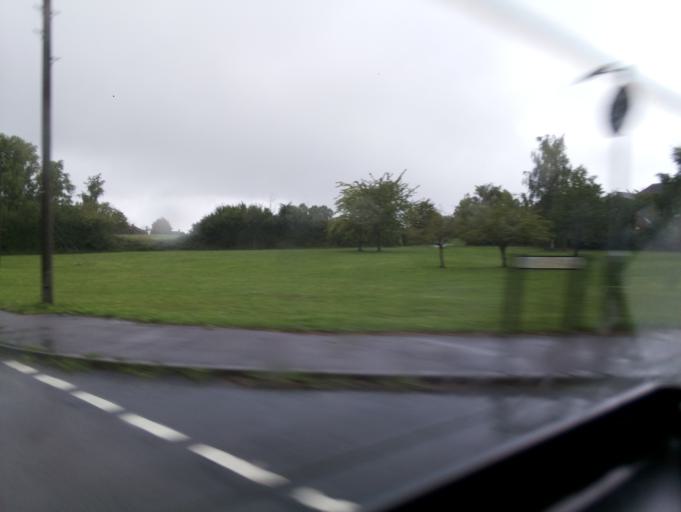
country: GB
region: England
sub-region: Gloucestershire
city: Tewkesbury
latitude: 51.9798
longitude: -2.1551
